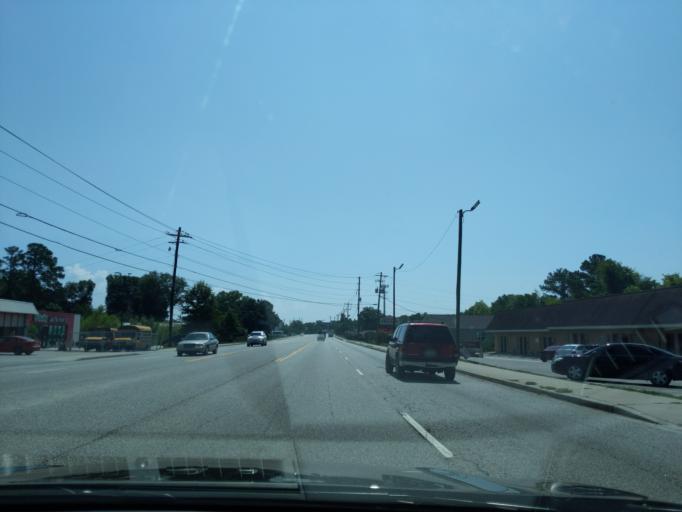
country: US
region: South Carolina
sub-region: Lexington County
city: Oak Grove
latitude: 33.9726
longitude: -81.1503
